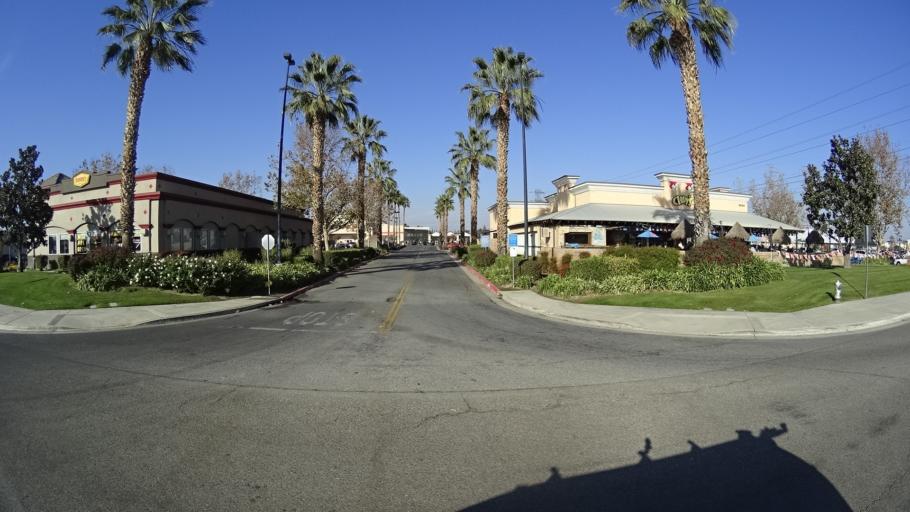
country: US
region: California
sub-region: Kern County
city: Greenacres
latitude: 35.3835
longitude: -119.0986
